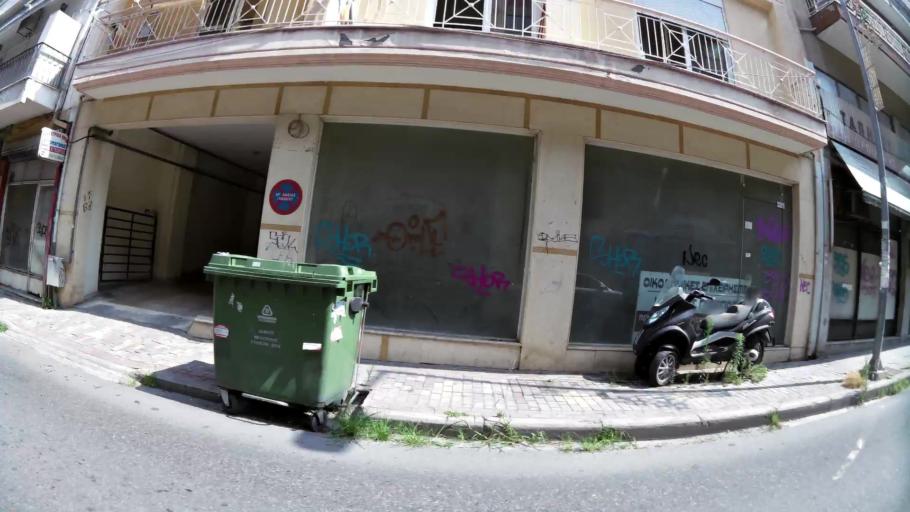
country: GR
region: Central Macedonia
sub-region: Nomos Thessalonikis
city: Sykies
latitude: 40.6492
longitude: 22.9412
